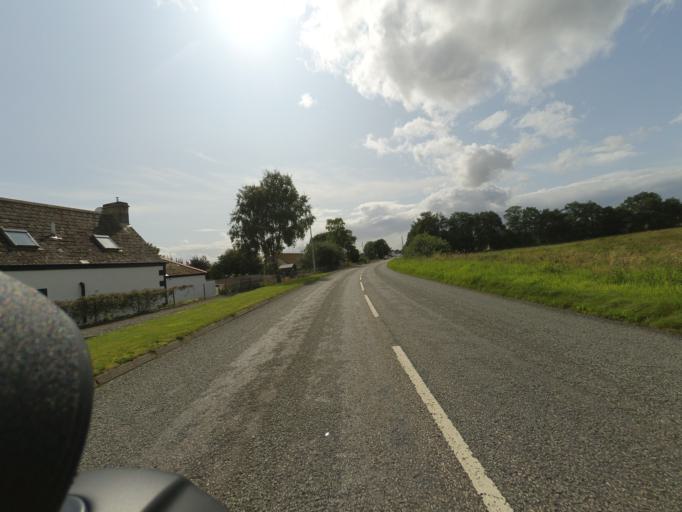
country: GB
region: Scotland
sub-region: Highland
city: Invergordon
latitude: 57.7245
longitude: -4.0978
